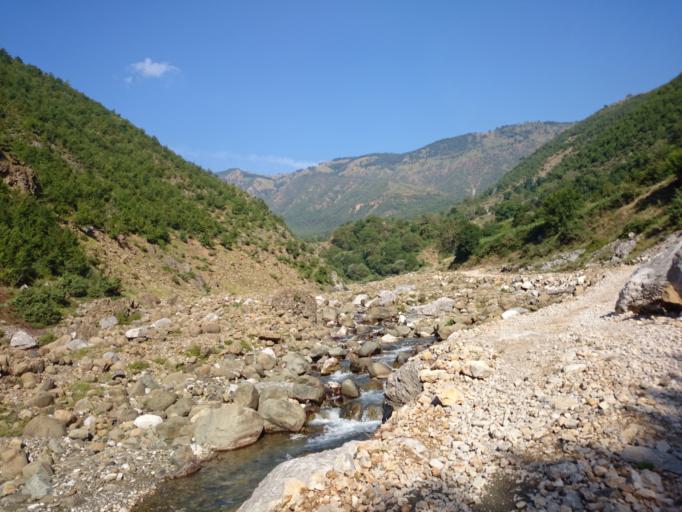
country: AL
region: Diber
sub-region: Rrethi i Dibres
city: Fushe-Lure
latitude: 41.7568
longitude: 20.2345
